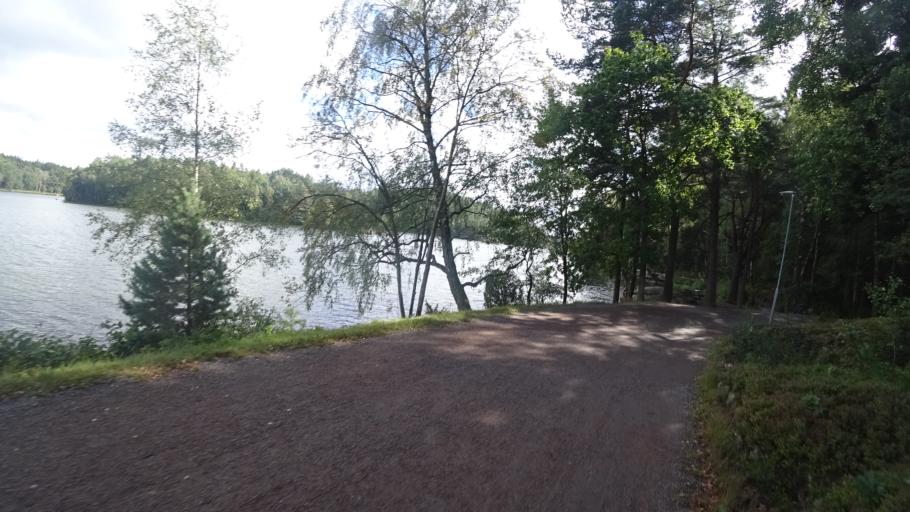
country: SE
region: Vaestra Goetaland
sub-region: Molndal
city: Moelndal
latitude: 57.6910
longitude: 12.0502
